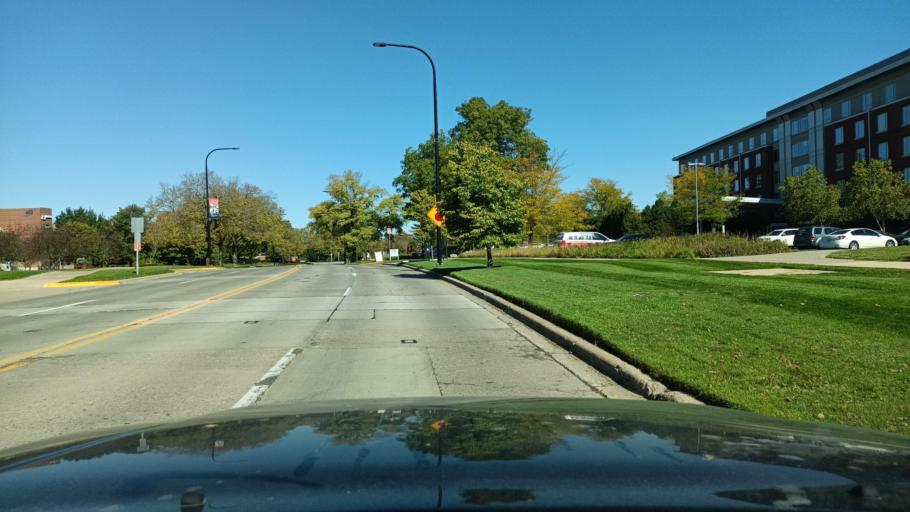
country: US
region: Illinois
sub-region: Champaign County
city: Champaign
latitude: 40.0927
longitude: -88.2382
